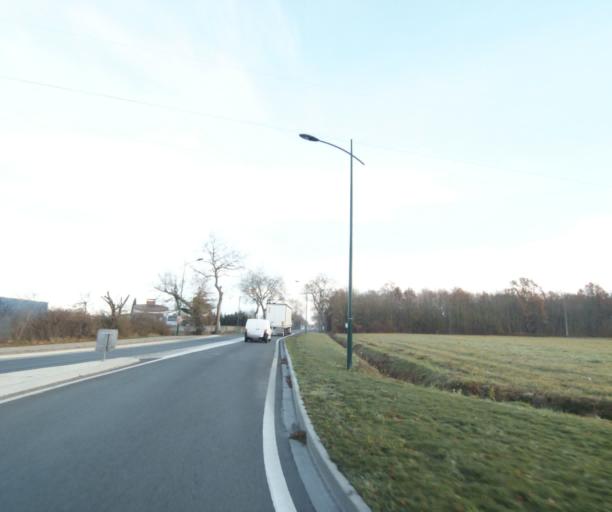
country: FR
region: Poitou-Charentes
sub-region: Departement de la Charente-Maritime
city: Fontcouverte
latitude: 45.7659
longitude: -0.5831
